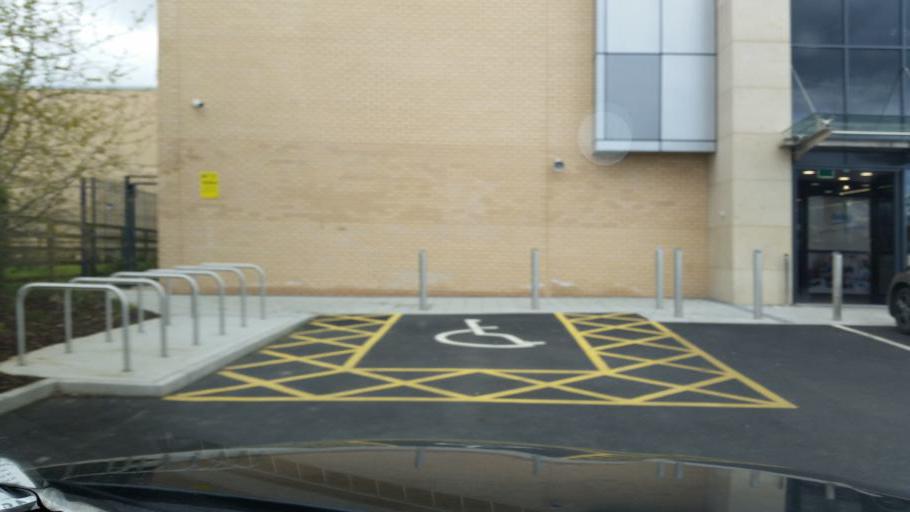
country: IE
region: Leinster
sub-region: Fingal County
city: Swords
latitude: 53.4443
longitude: -6.2232
